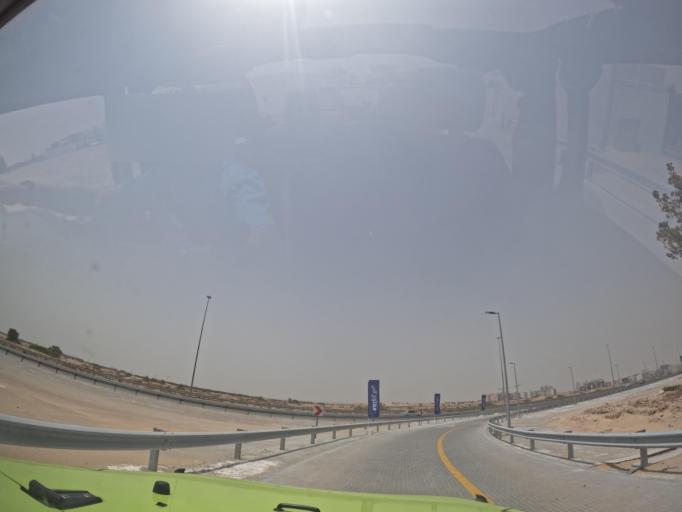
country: AE
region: Dubai
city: Dubai
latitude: 25.0895
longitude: 55.3564
